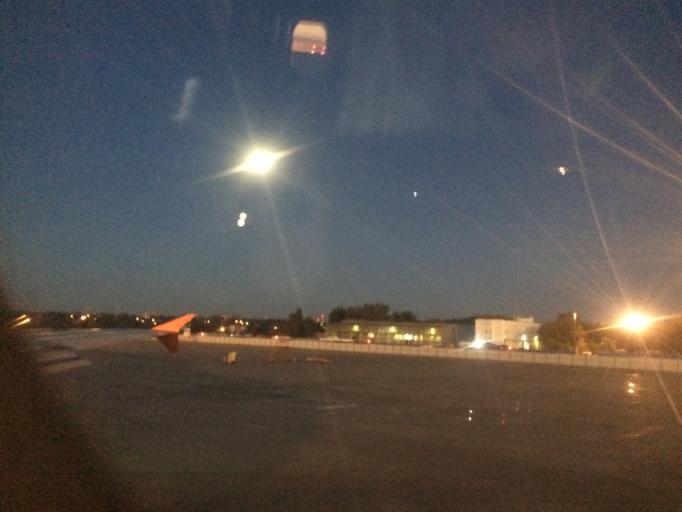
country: RU
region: Rostov
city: Aksay
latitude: 47.2529
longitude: 39.8047
